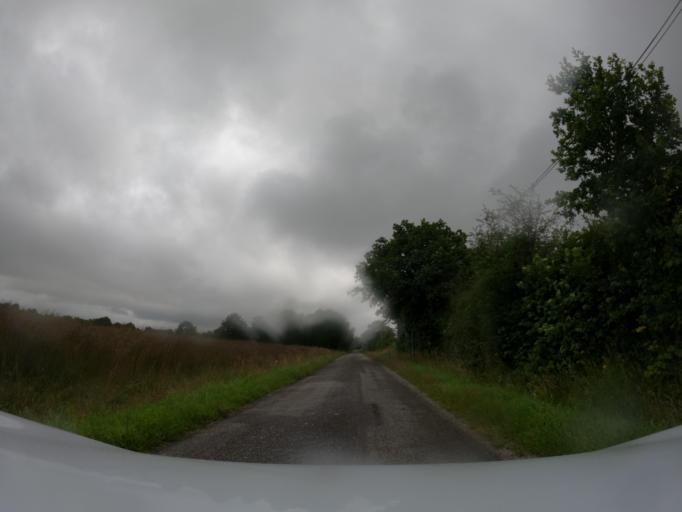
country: FR
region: Pays de la Loire
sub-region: Departement de la Loire-Atlantique
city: Saint-Mars-du-Desert
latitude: 47.3840
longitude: -1.4122
